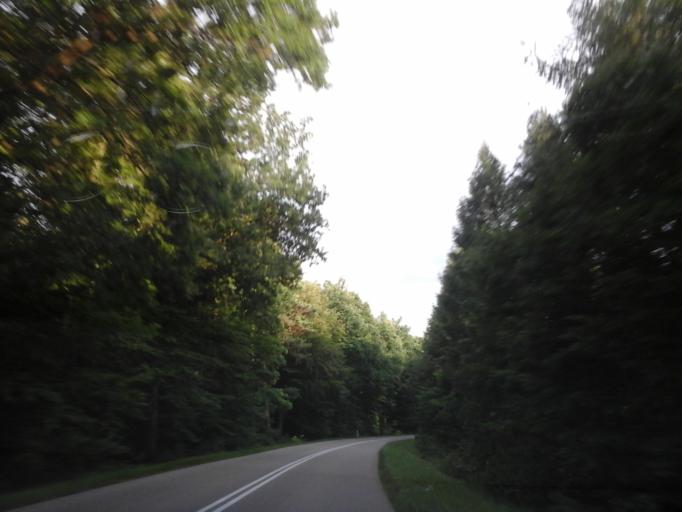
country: PL
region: West Pomeranian Voivodeship
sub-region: Powiat kamienski
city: Golczewo
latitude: 53.7432
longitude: 15.0133
